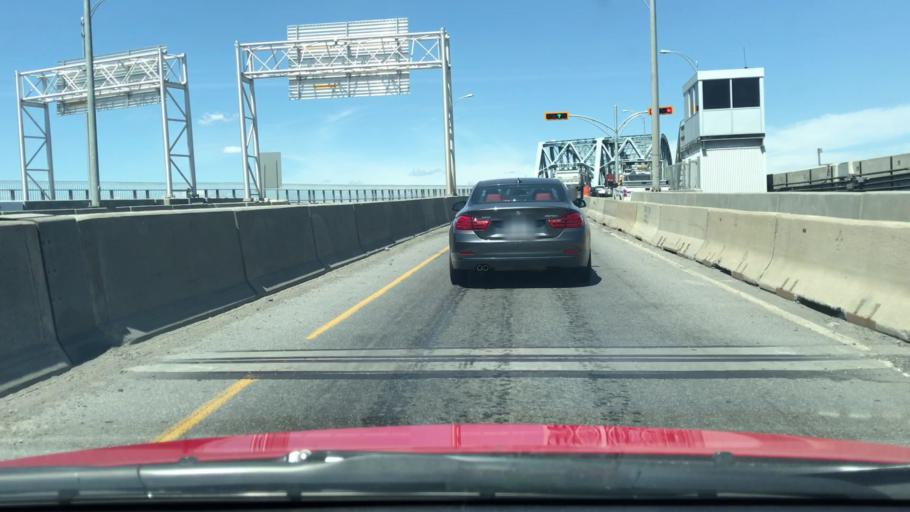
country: CA
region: Quebec
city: Montreal-Ouest
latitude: 45.4080
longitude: -73.6594
